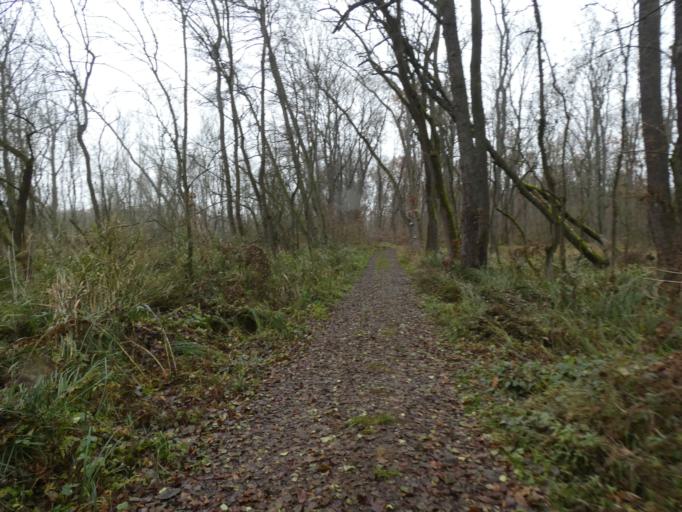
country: HU
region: Pest
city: Ocsa
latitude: 47.2618
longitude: 19.2326
